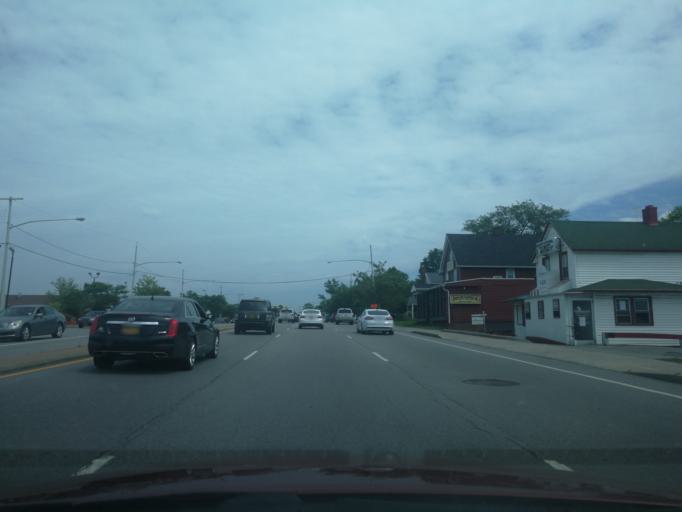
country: US
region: New York
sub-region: Monroe County
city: Greece
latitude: 43.2050
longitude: -77.6660
